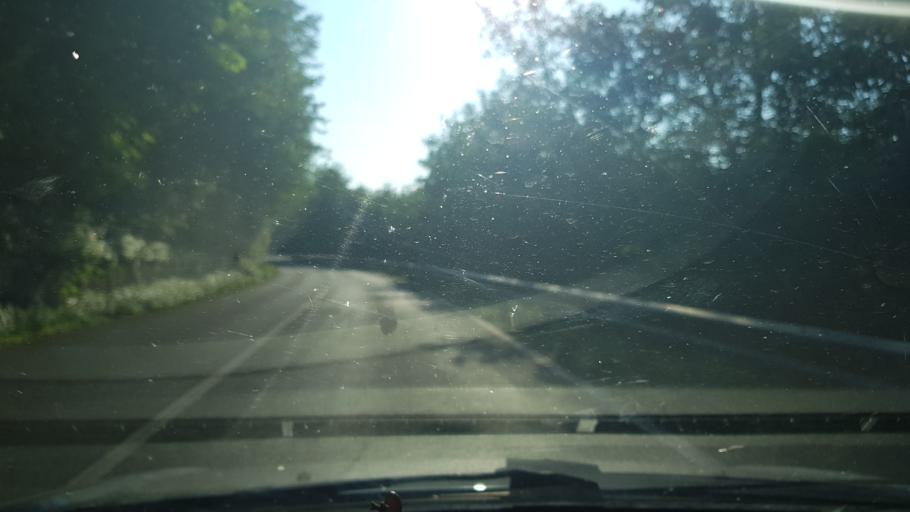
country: IT
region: Friuli Venezia Giulia
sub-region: Provincia di Gorizia
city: Savogna d'Isonzo
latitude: 45.8995
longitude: 13.5612
